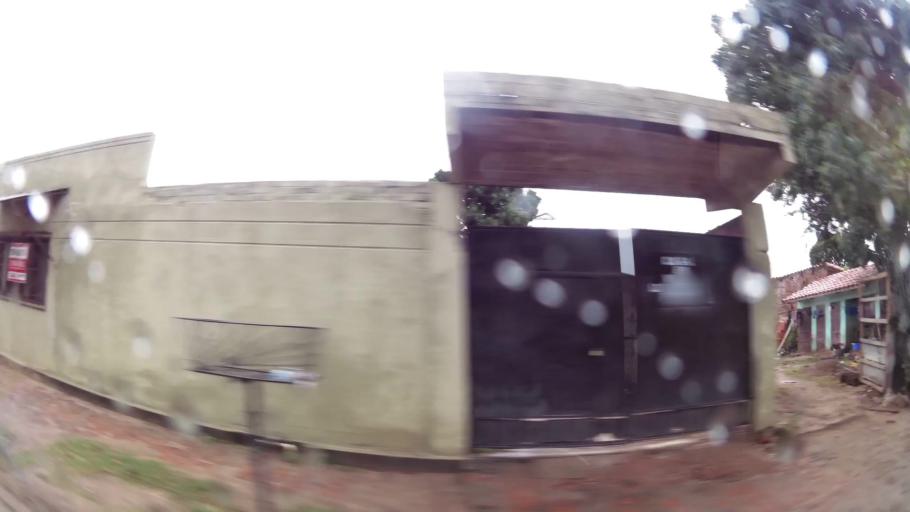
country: BO
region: Santa Cruz
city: Santa Cruz de la Sierra
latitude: -17.7579
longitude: -63.1183
